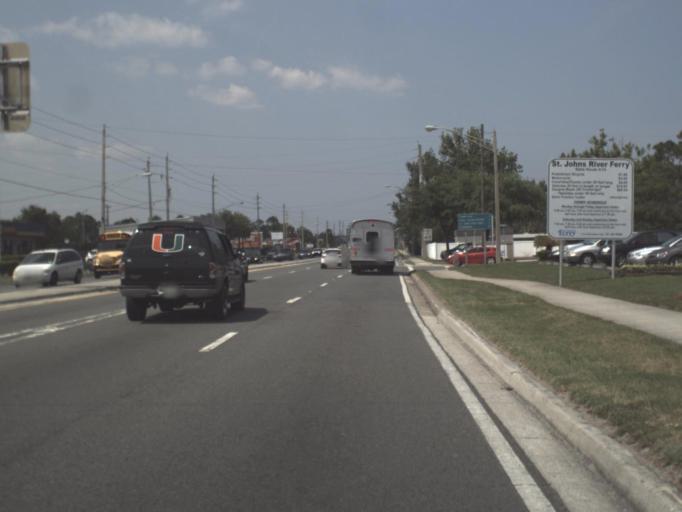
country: US
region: Florida
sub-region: Duval County
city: Atlantic Beach
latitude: 30.3287
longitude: -81.4176
